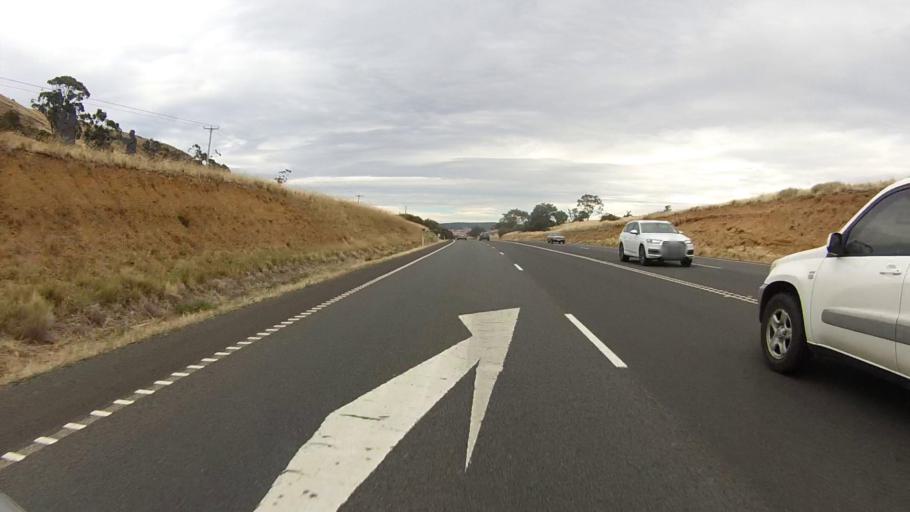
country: AU
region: Tasmania
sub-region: Brighton
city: Bridgewater
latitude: -42.3357
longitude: 147.3430
